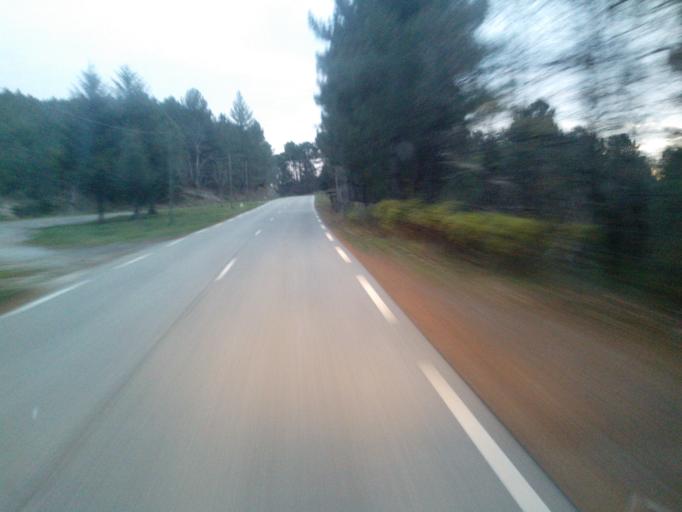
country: FR
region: Languedoc-Roussillon
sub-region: Departement du Gard
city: Saint-Jean-du-Gard
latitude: 44.1447
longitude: 3.7765
